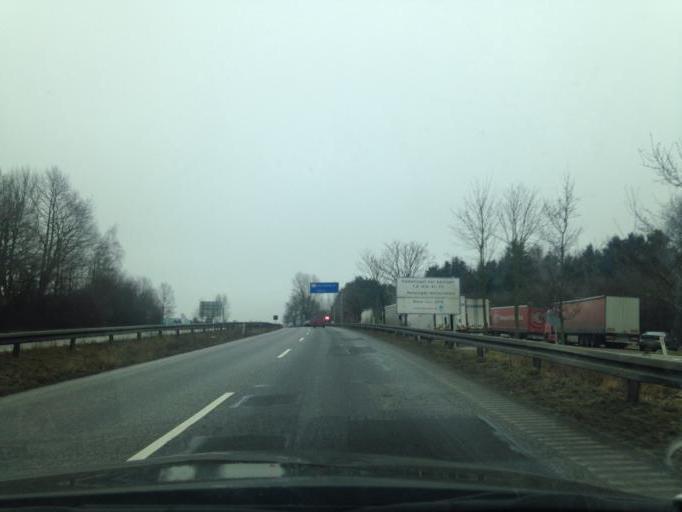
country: DK
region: Capital Region
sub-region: Horsholm Kommune
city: Horsholm
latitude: 55.8665
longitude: 12.4842
